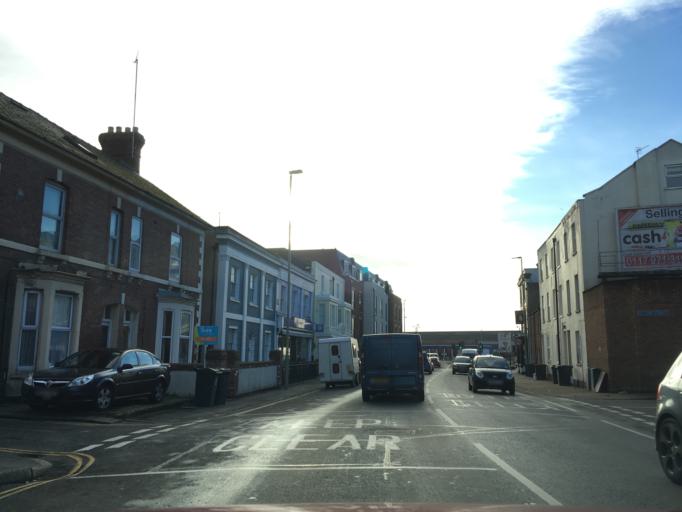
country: GB
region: England
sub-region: Gloucestershire
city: Gloucester
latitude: 51.8596
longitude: -2.2507
